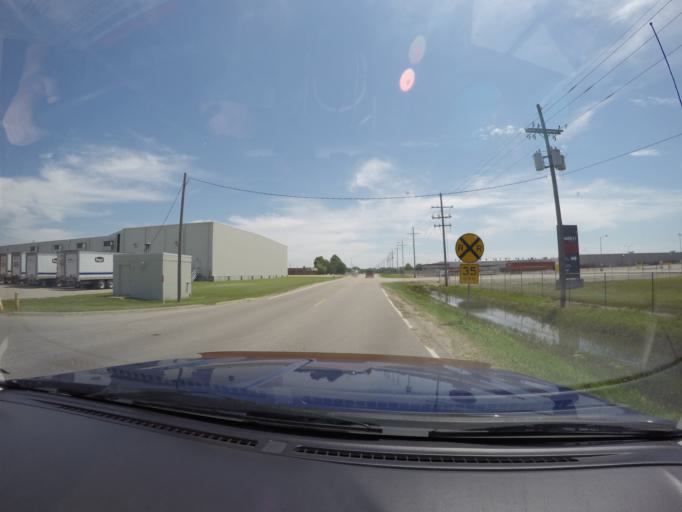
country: US
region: Nebraska
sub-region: Hall County
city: Grand Island
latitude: 40.9024
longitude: -98.3878
